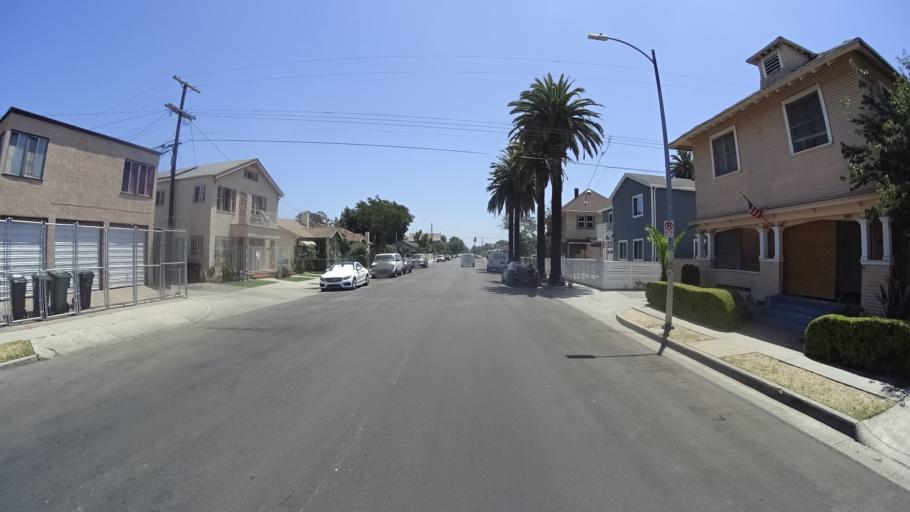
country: US
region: California
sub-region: Los Angeles County
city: View Park-Windsor Hills
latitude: 34.0291
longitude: -118.3036
